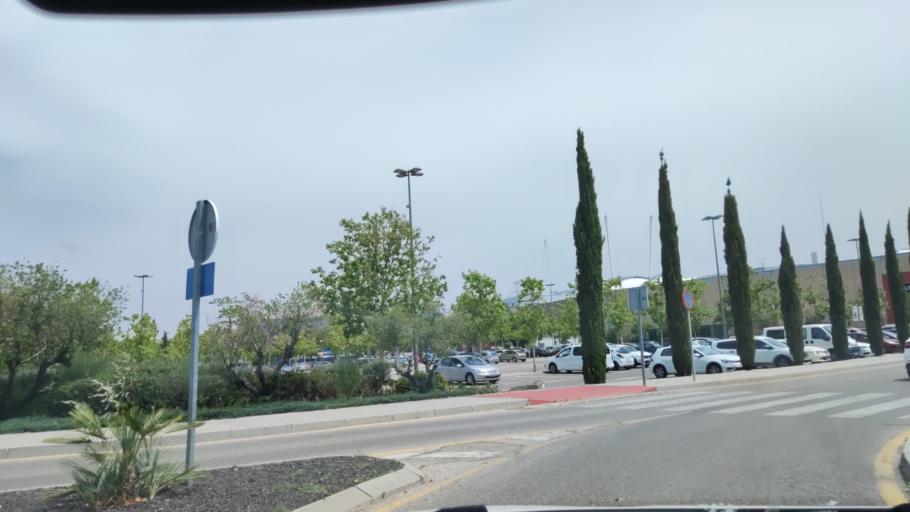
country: ES
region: Madrid
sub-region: Provincia de Madrid
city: Arroyomolinos
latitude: 40.3011
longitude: -3.9270
